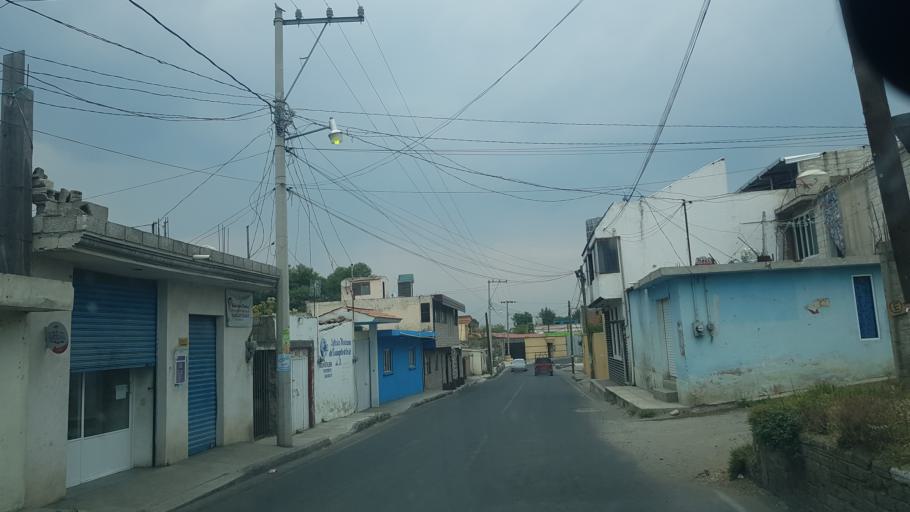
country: MX
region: Puebla
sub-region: Huejotzingo
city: San Mateo Capultitlan
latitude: 19.1995
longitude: -98.4394
